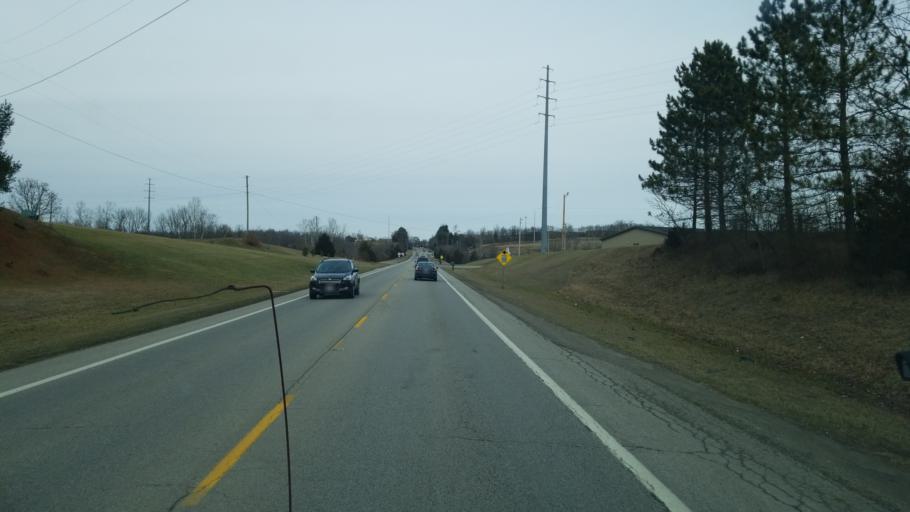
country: US
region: Ohio
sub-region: Highland County
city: Hillsboro
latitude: 39.1805
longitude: -83.6194
